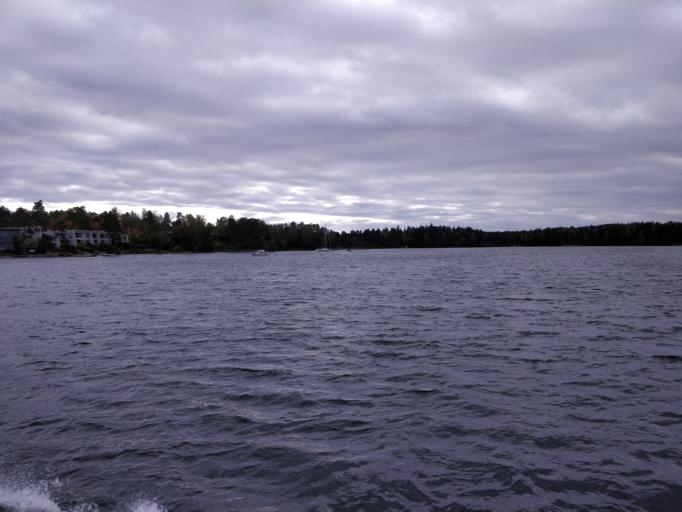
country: FI
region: Uusimaa
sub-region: Helsinki
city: Vantaa
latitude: 60.1750
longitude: 25.0802
